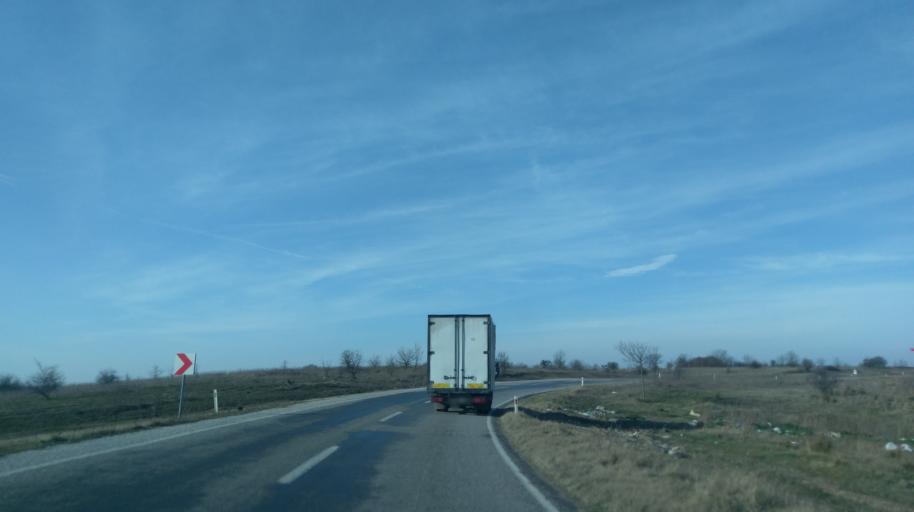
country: TR
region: Edirne
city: Copkoy
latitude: 41.3070
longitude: 26.8441
